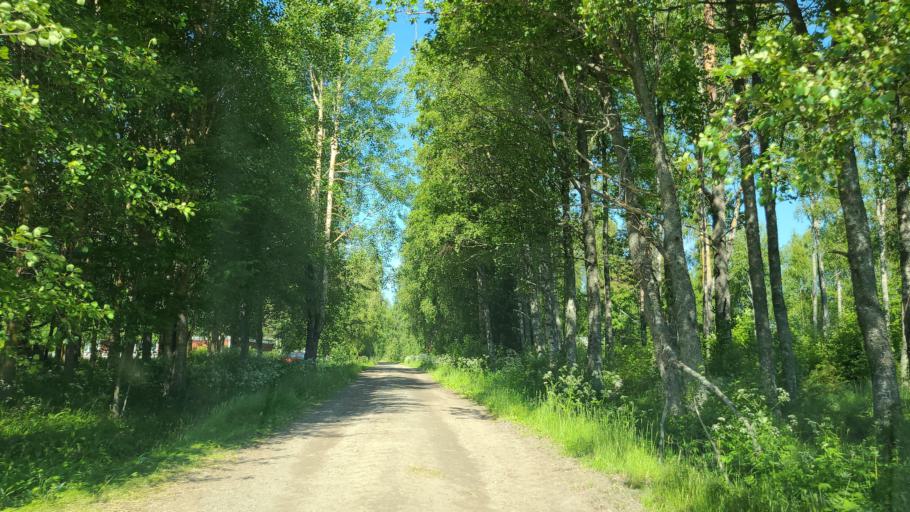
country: SE
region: Vaesterbotten
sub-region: Robertsfors Kommun
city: Robertsfors
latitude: 64.0872
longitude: 20.8510
